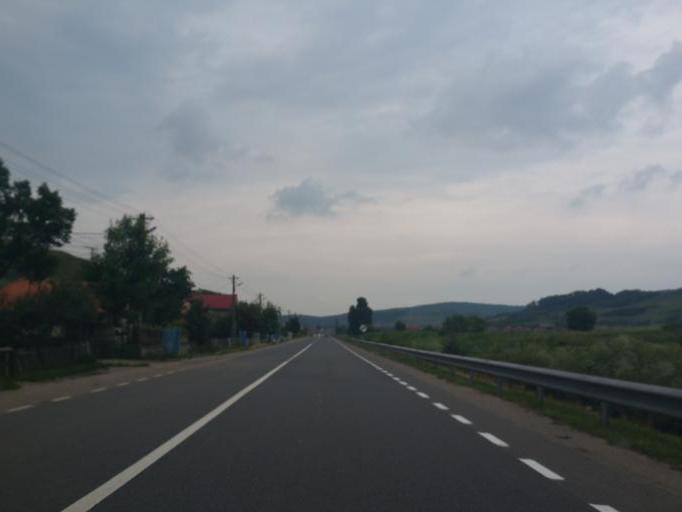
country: RO
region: Cluj
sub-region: Comuna Sanpaul
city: Sanpaul
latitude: 46.8642
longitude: 23.4104
